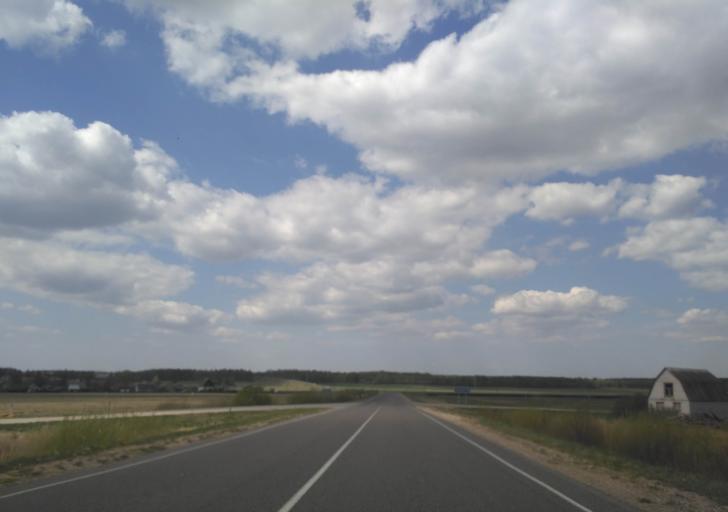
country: BY
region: Minsk
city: Vilyeyka
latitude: 54.5187
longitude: 26.9765
